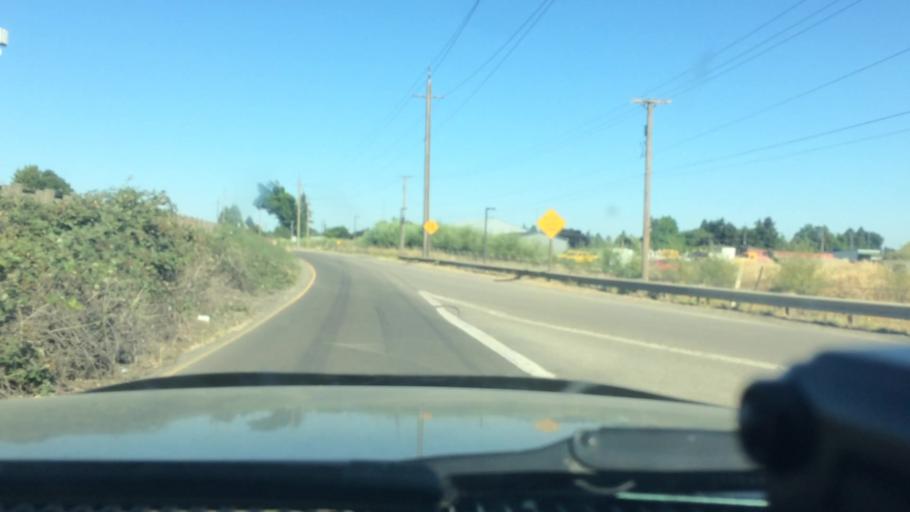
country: US
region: Oregon
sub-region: Lane County
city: Eugene
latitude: 44.0973
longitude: -123.1105
